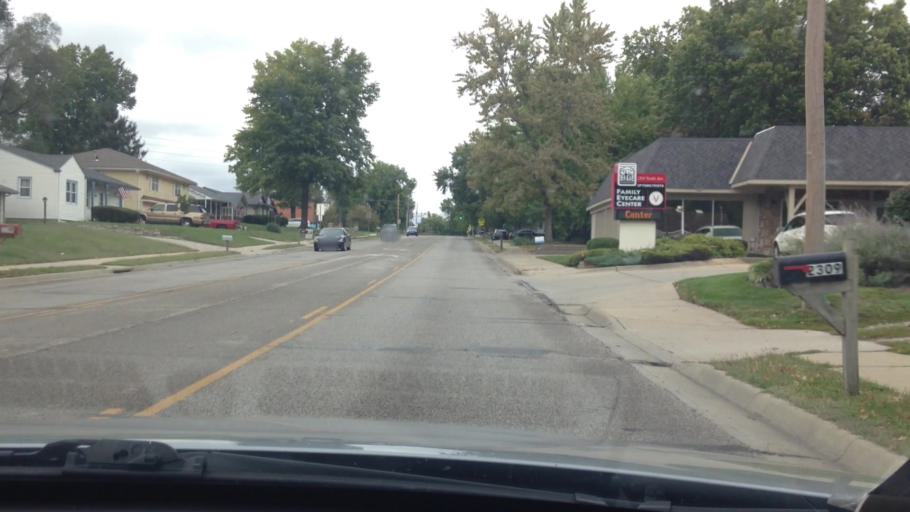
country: US
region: Kansas
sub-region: Leavenworth County
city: Leavenworth
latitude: 39.2935
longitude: -94.9277
